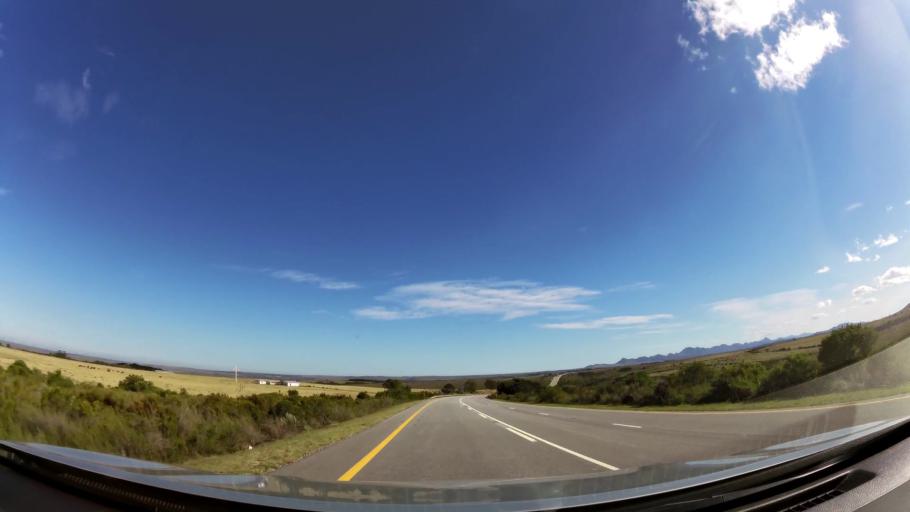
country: ZA
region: Eastern Cape
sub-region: Cacadu District Municipality
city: Kruisfontein
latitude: -34.0037
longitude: 24.6785
